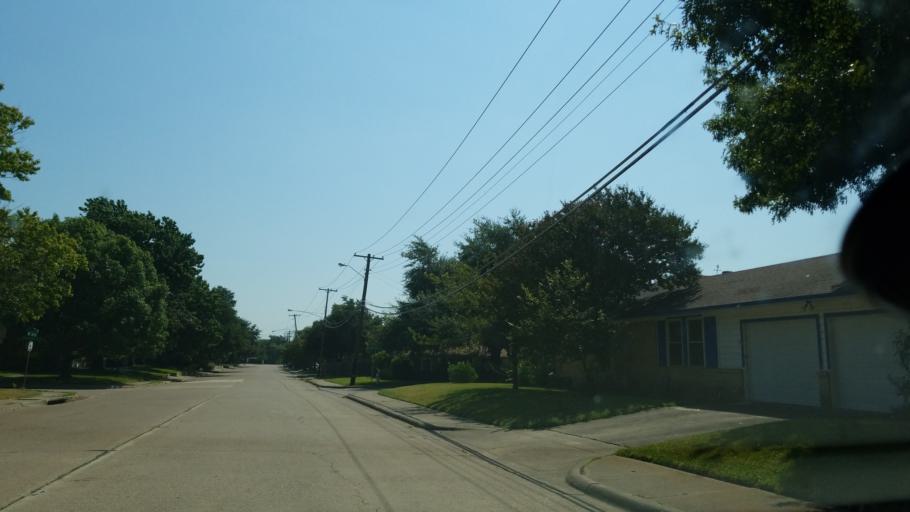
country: US
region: Texas
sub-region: Dallas County
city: Garland
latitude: 32.8716
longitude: -96.7037
